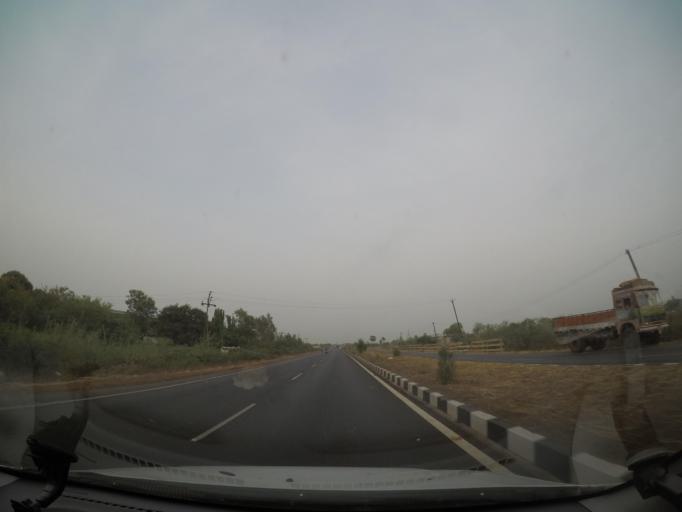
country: IN
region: Andhra Pradesh
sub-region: Krishna
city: Gannavaram
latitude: 16.6210
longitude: 80.9321
